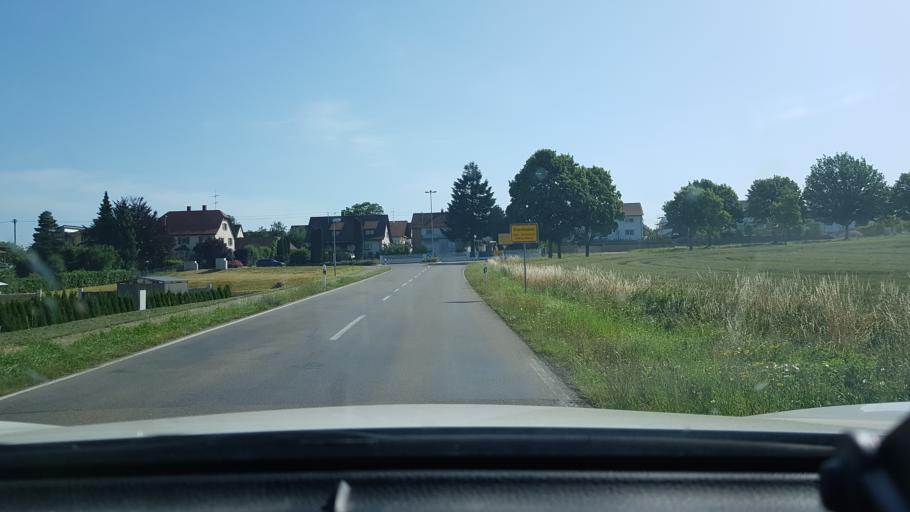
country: DE
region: Baden-Wuerttemberg
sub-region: Tuebingen Region
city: Schwendi
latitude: 48.2065
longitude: 9.9618
